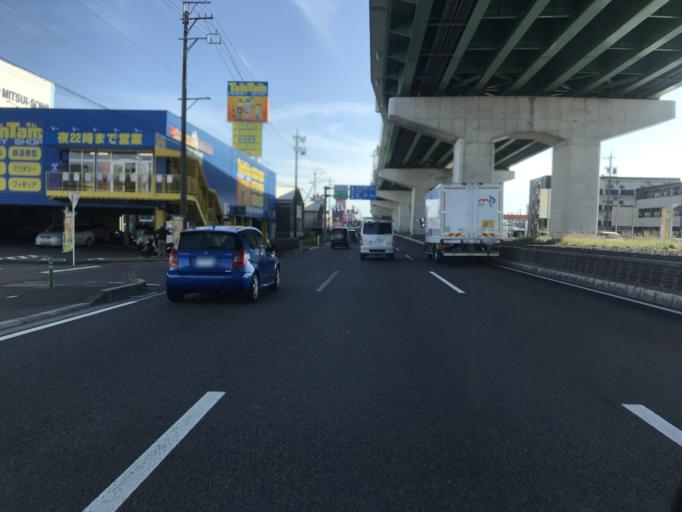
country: JP
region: Aichi
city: Iwakura
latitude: 35.2408
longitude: 136.8471
